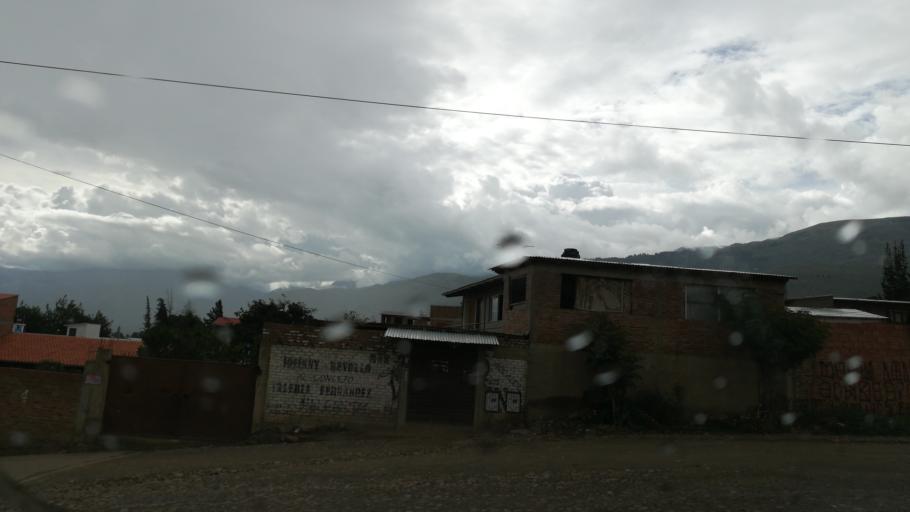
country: BO
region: Cochabamba
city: Cochabamba
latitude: -17.3335
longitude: -66.1968
